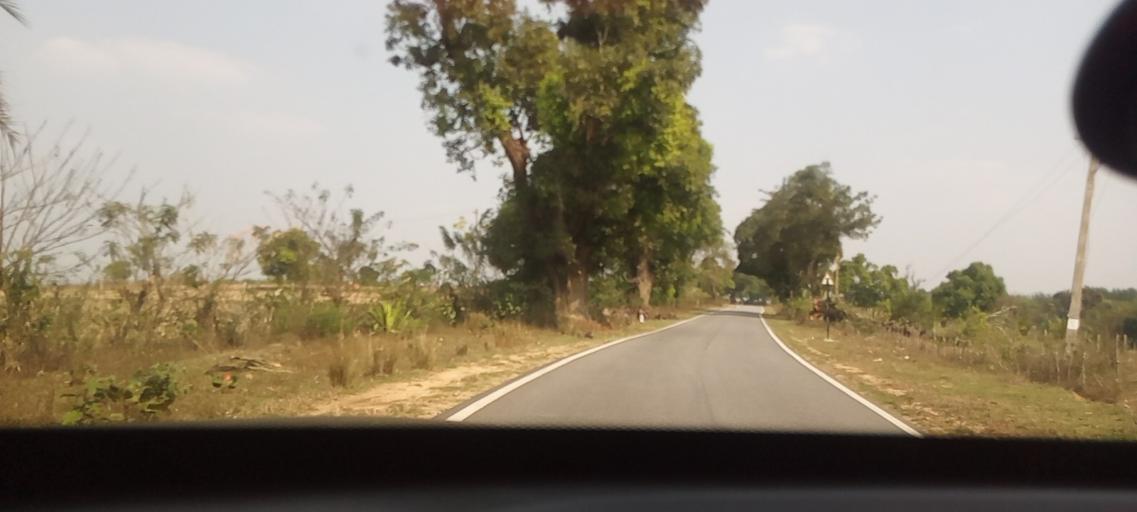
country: IN
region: Karnataka
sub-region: Hassan
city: Belur
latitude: 13.1800
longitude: 75.8070
